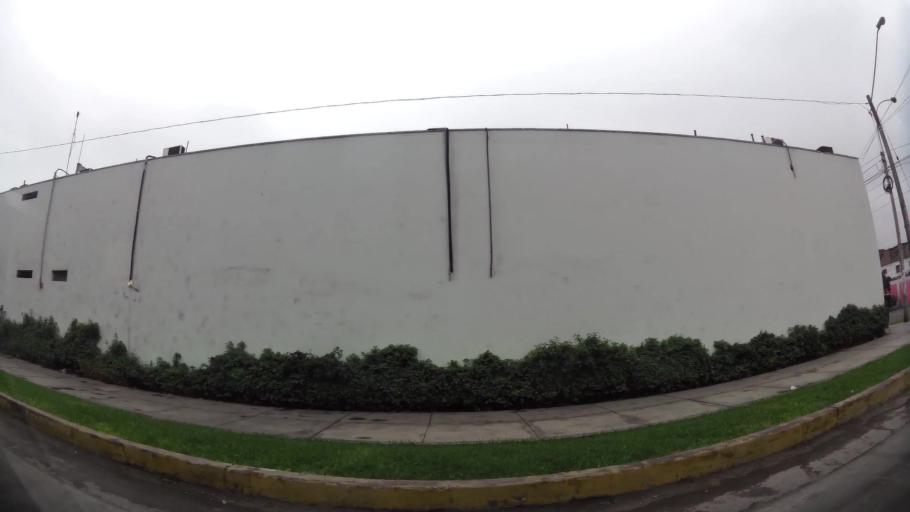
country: PE
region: Lima
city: Lima
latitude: -12.0637
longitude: -77.0205
